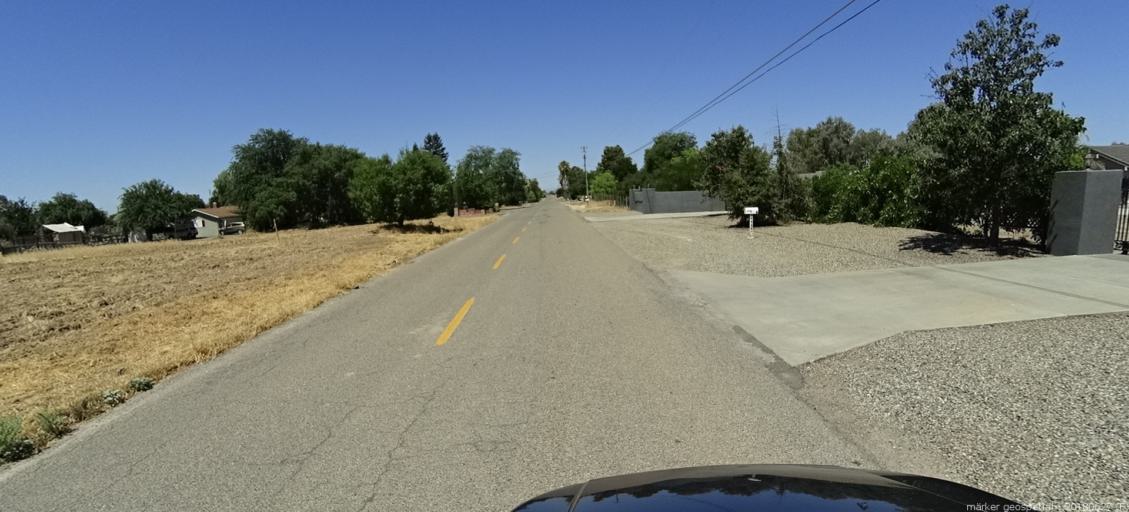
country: US
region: California
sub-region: Madera County
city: Bonadelle Ranchos-Madera Ranchos
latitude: 36.9352
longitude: -119.8983
